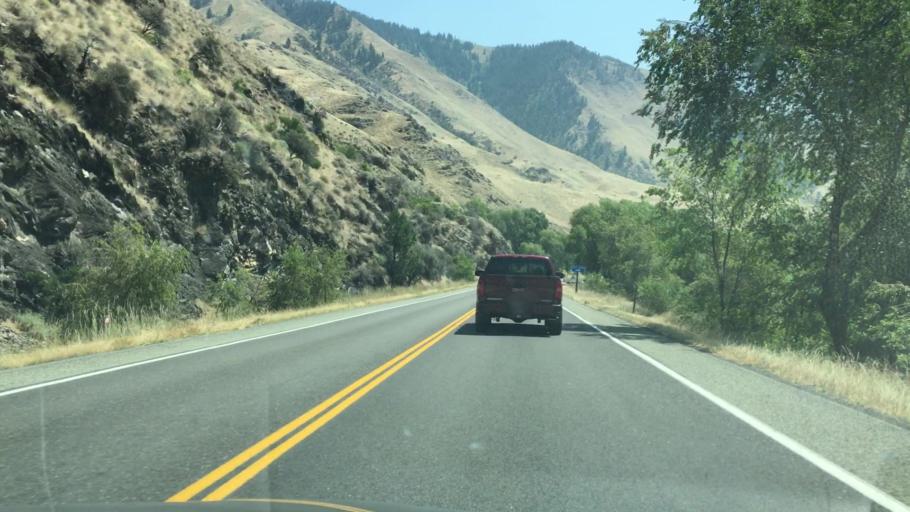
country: US
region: Idaho
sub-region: Valley County
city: McCall
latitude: 45.3453
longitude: -116.3527
